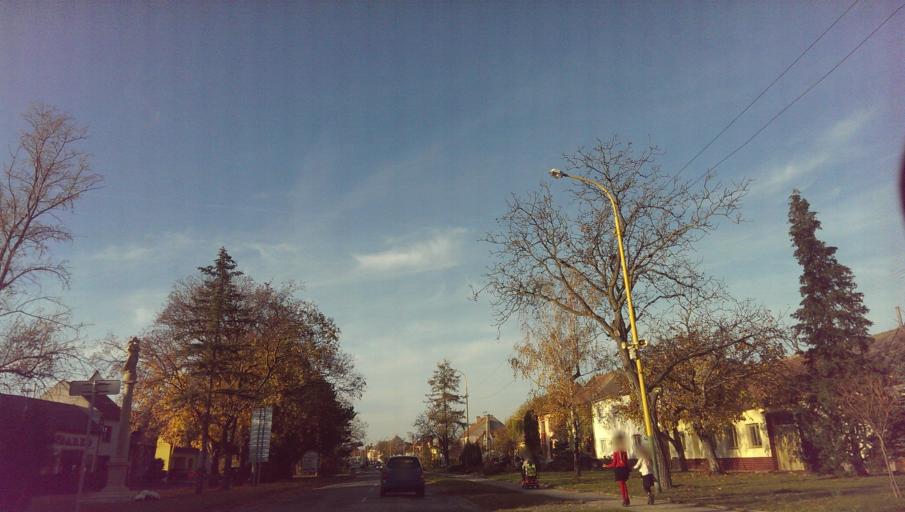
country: CZ
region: Zlin
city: Ostrozska Lhota
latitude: 48.9472
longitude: 17.4617
